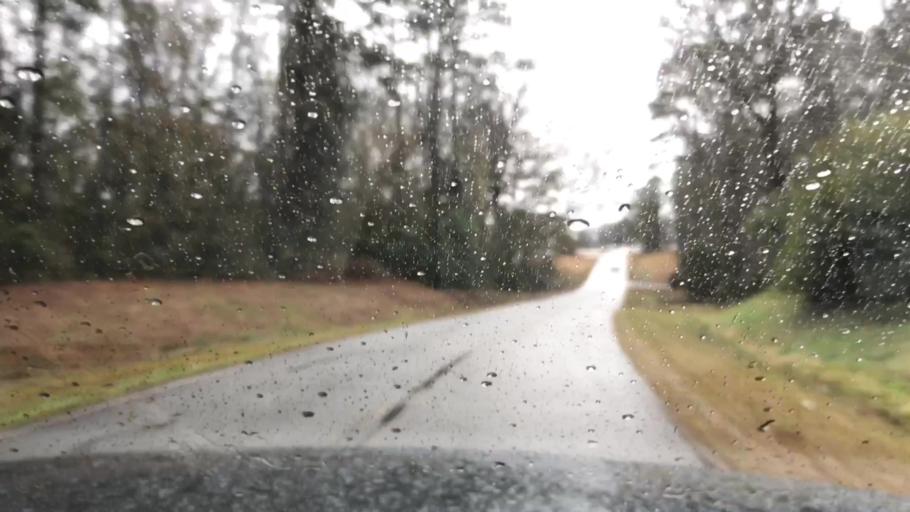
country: US
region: Georgia
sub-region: Morgan County
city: Madison
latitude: 33.5835
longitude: -83.4874
